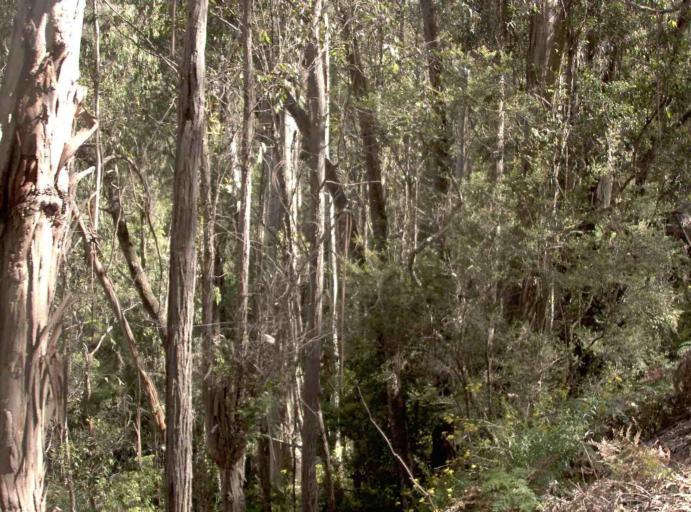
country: AU
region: New South Wales
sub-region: Bombala
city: Bombala
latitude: -37.2987
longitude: 148.7082
